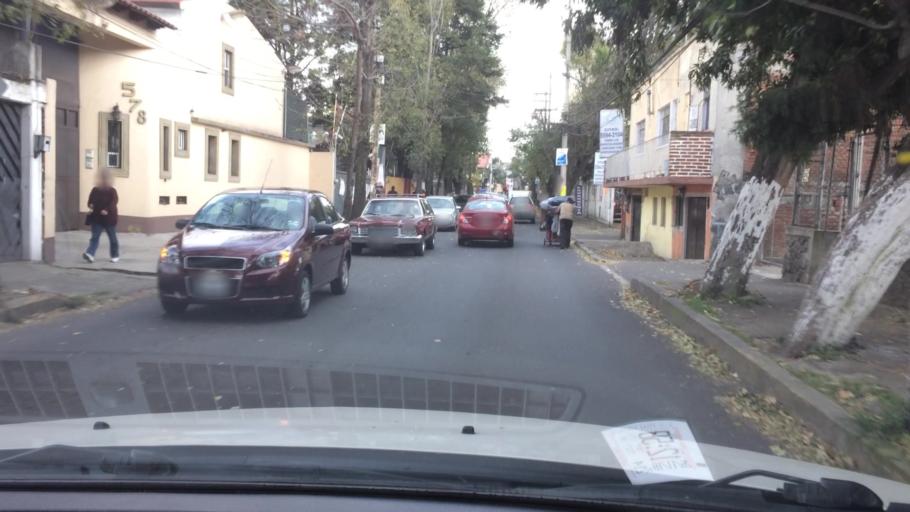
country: MX
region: Mexico City
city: Tlalpan
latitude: 19.2807
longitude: -99.1393
